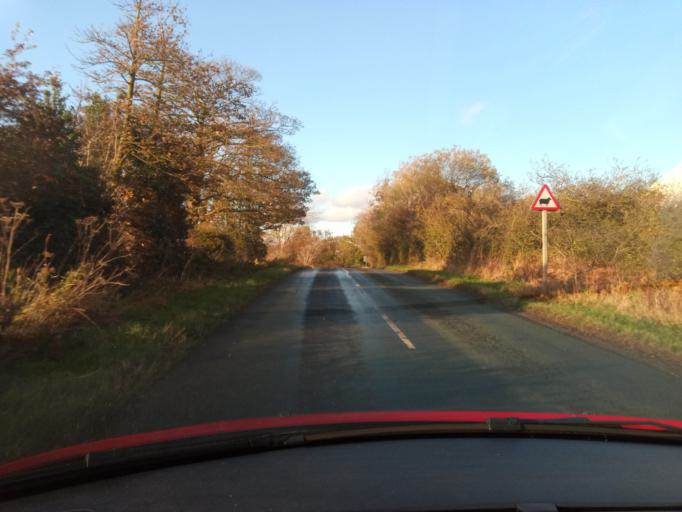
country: GB
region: England
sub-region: County Durham
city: Hamsterley
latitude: 54.6627
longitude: -1.8099
